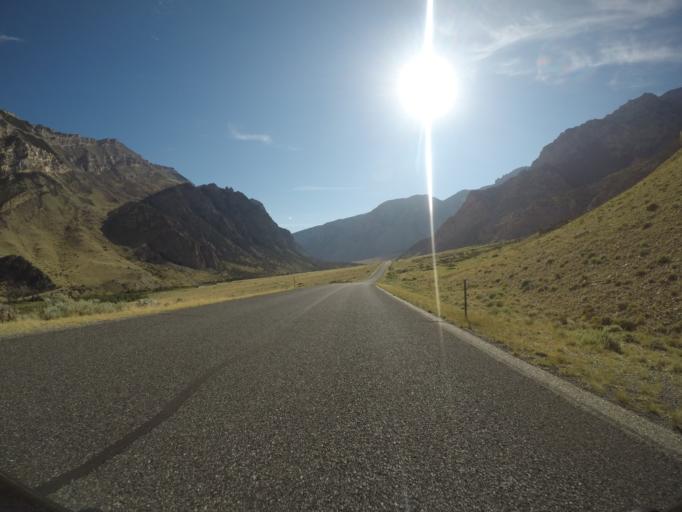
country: US
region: Montana
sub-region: Carbon County
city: Red Lodge
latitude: 44.8470
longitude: -109.3079
